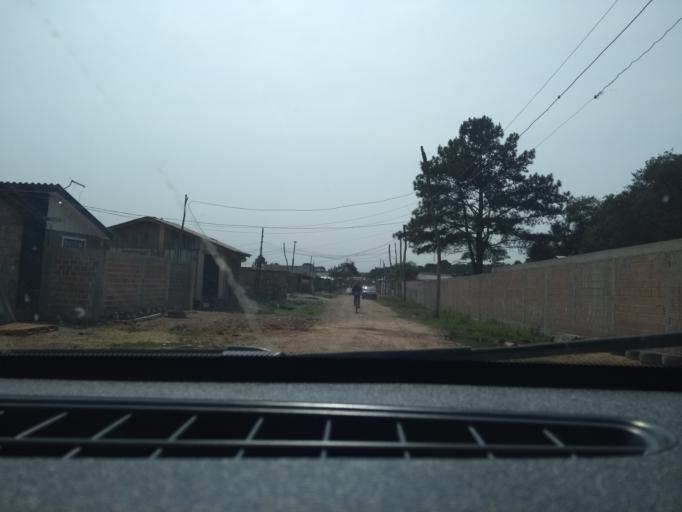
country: BR
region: Parana
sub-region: Araucaria
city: Araucaria
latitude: -25.6261
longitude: -49.3579
